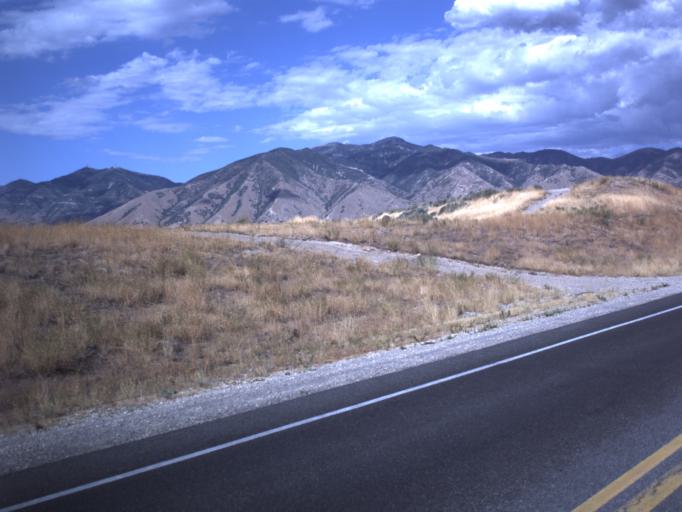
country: US
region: Utah
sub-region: Tooele County
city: Tooele
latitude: 40.5509
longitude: -112.3117
